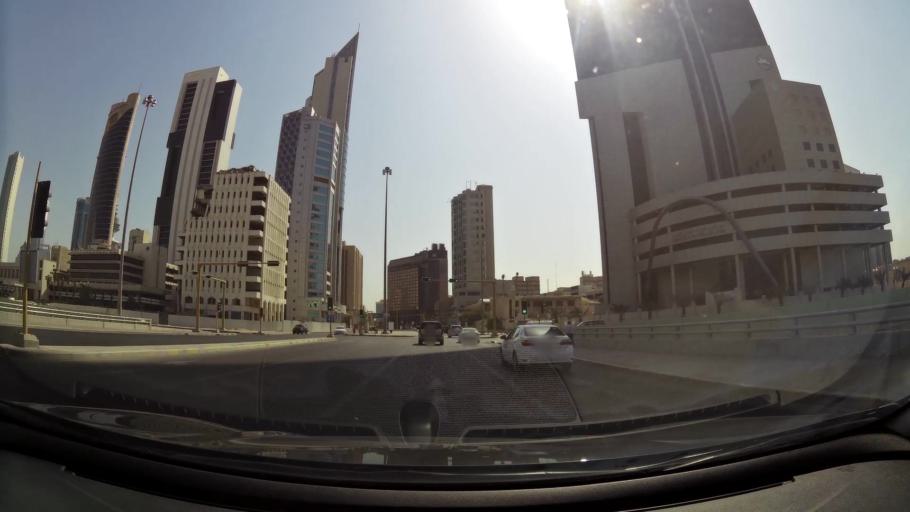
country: KW
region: Al Asimah
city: Kuwait City
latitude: 29.3673
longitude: 47.9641
